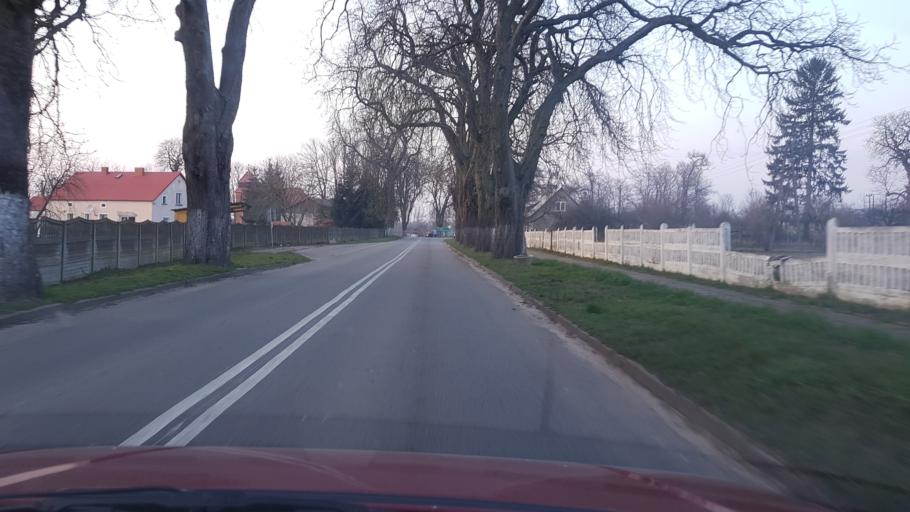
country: PL
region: West Pomeranian Voivodeship
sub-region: Powiat lobeski
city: Radowo Male
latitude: 53.6839
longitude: 15.4216
